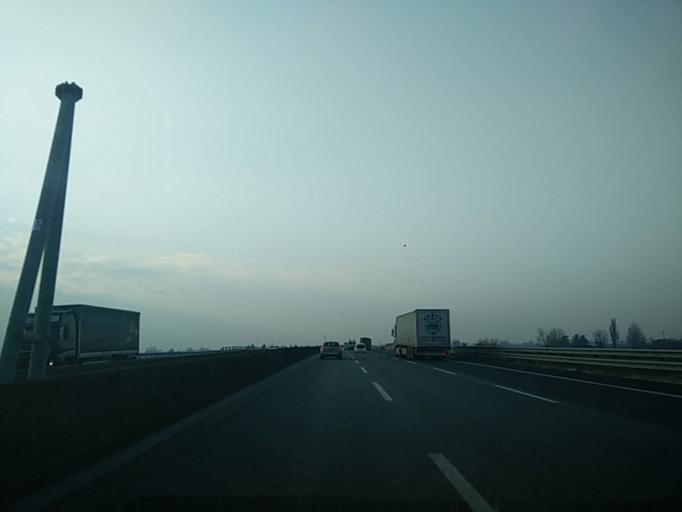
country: IT
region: Emilia-Romagna
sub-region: Provincia di Ravenna
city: Solarolo
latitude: 44.3502
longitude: 11.8280
